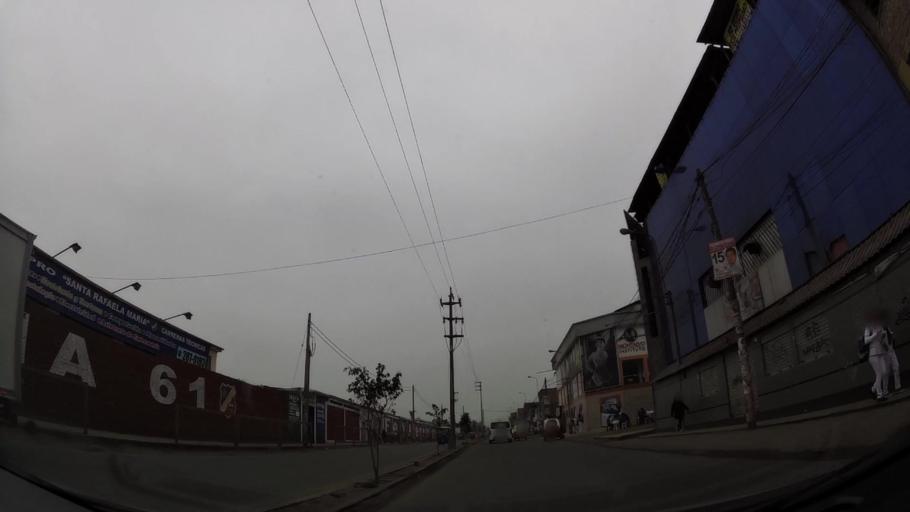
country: PE
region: Lima
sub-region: Lima
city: Surco
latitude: -12.2197
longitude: -76.9329
